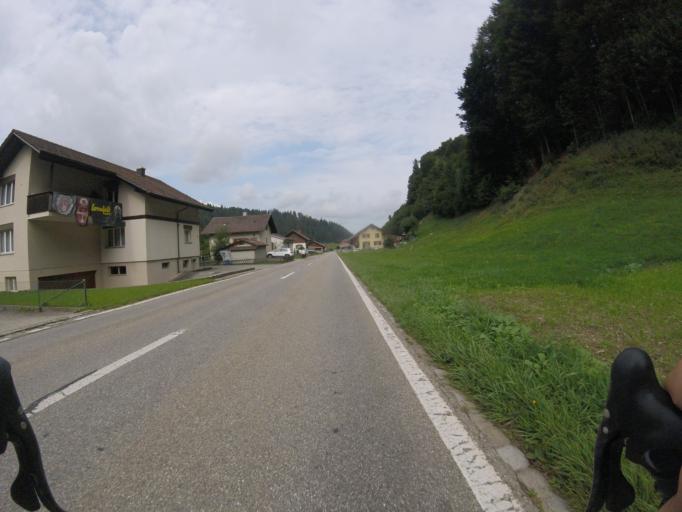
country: CH
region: Bern
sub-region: Emmental District
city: Lutzelfluh
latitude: 46.9935
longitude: 7.6854
